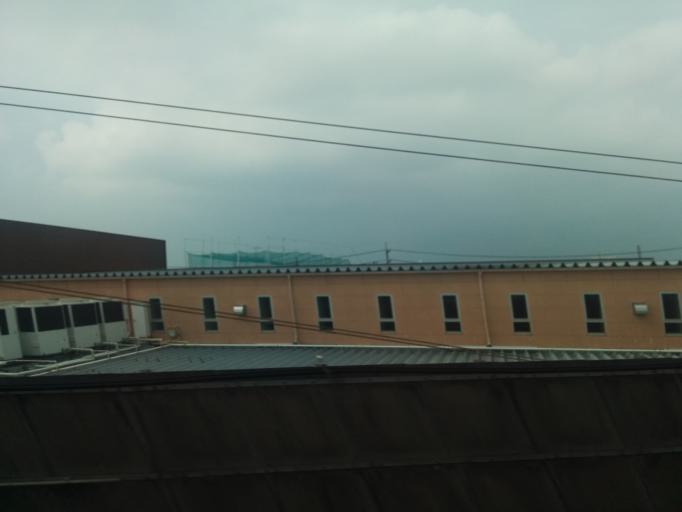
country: JP
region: Aichi
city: Chiryu
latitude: 35.0007
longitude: 137.0222
